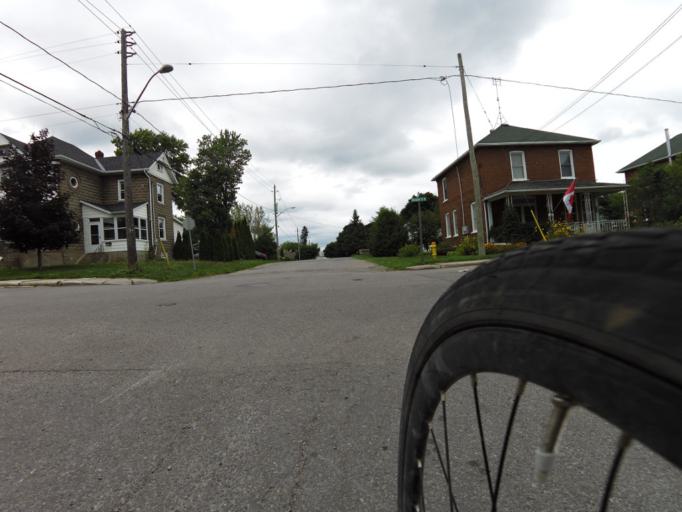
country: CA
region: Ontario
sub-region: Lanark County
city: Smiths Falls
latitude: 44.9001
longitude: -76.0263
